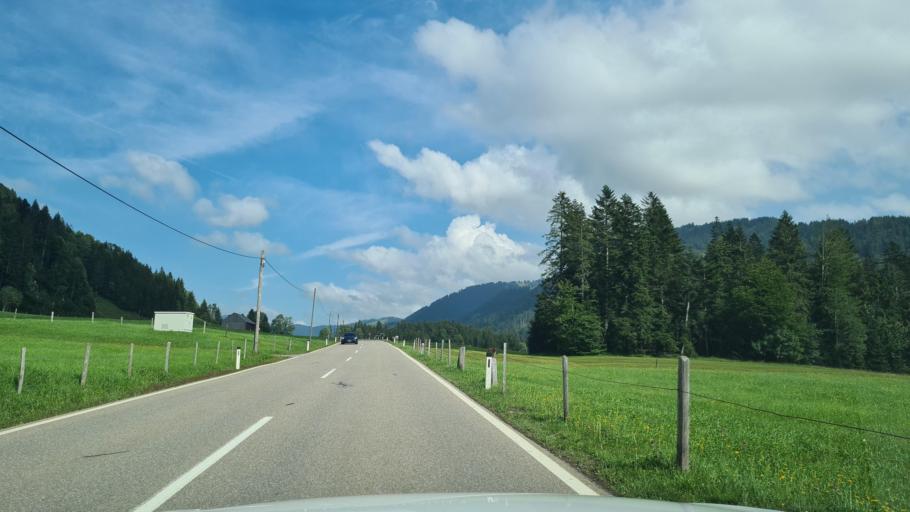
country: AT
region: Vorarlberg
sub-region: Politischer Bezirk Bregenz
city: Sibratsgfall
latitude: 47.4480
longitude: 10.0149
